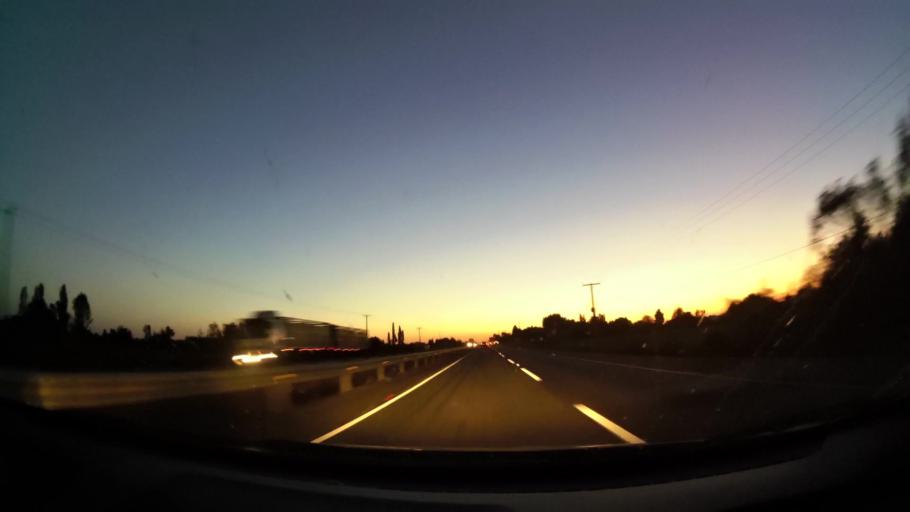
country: CL
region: Biobio
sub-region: Provincia de Nuble
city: San Carlos
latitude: -36.3519
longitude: -71.8628
